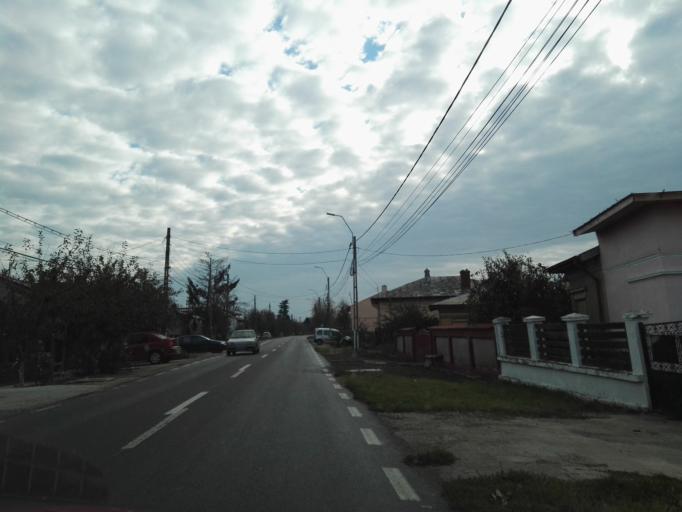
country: RO
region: Ilfov
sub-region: Comuna Magurele
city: Alunisu
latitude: 44.3416
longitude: 26.0482
